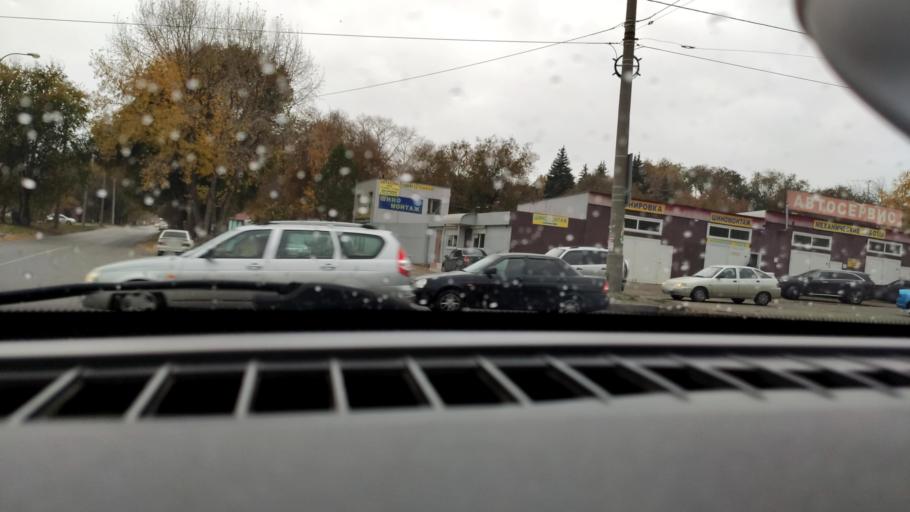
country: RU
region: Samara
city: Samara
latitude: 53.2255
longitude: 50.2333
